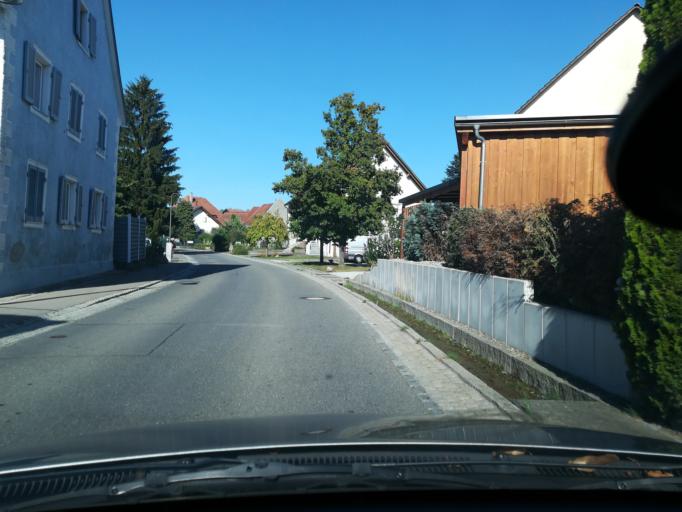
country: DE
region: Baden-Wuerttemberg
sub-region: Freiburg Region
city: Moos
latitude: 47.7177
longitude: 8.8941
